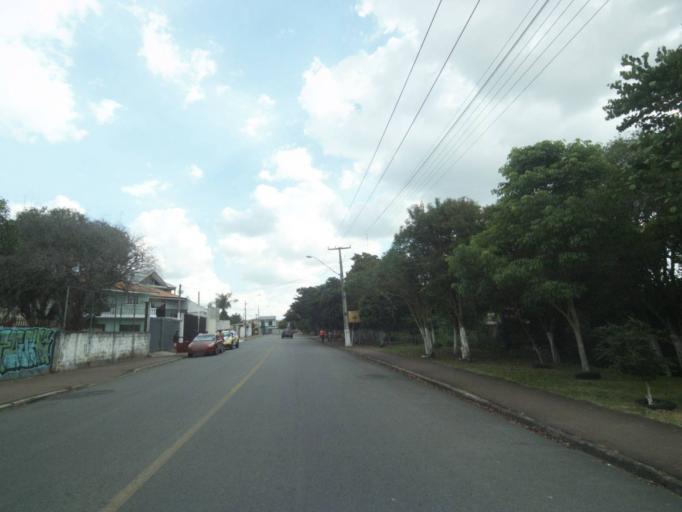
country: BR
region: Parana
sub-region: Sao Jose Dos Pinhais
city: Sao Jose dos Pinhais
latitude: -25.5287
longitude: -49.2703
